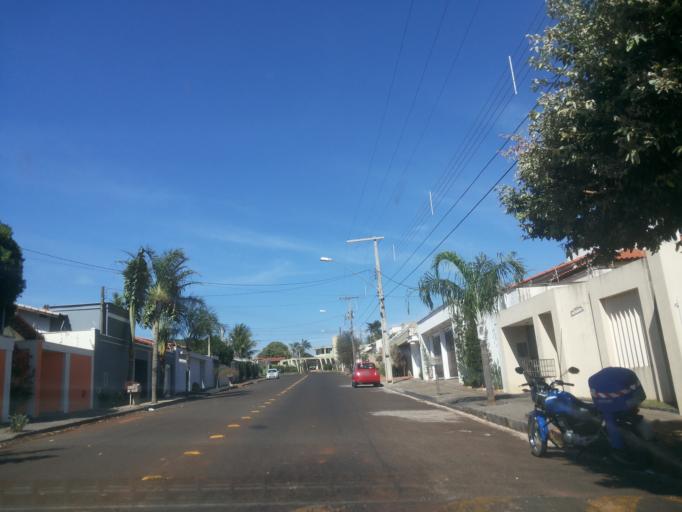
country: BR
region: Minas Gerais
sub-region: Ituiutaba
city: Ituiutaba
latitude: -18.9870
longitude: -49.4609
